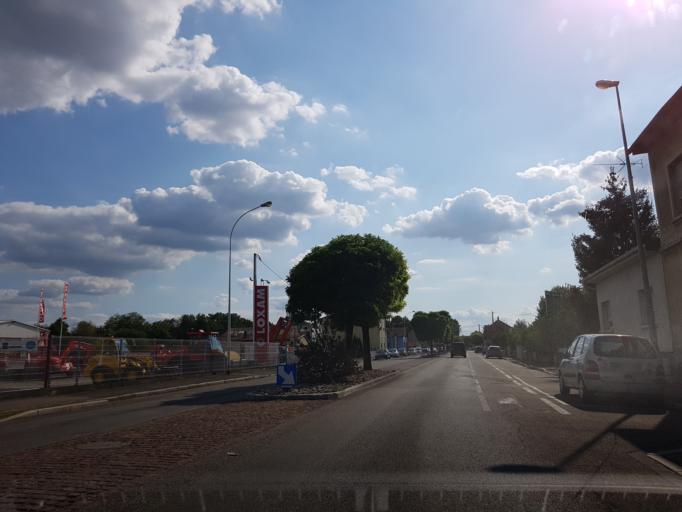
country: FR
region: Alsace
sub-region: Departement du Haut-Rhin
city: Riedisheim
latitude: 47.7619
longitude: 7.3723
